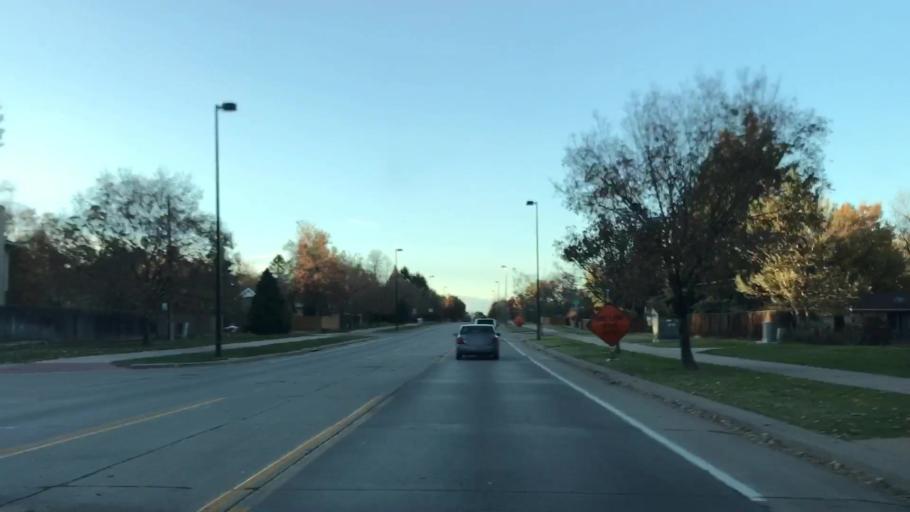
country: US
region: Colorado
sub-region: Arapahoe County
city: Glendale
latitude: 39.6623
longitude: -104.8876
